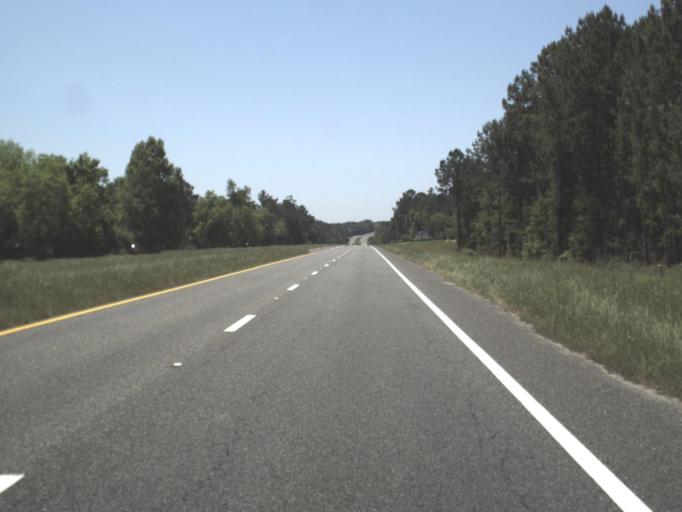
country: US
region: Florida
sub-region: Jefferson County
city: Monticello
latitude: 30.5076
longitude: -83.8774
